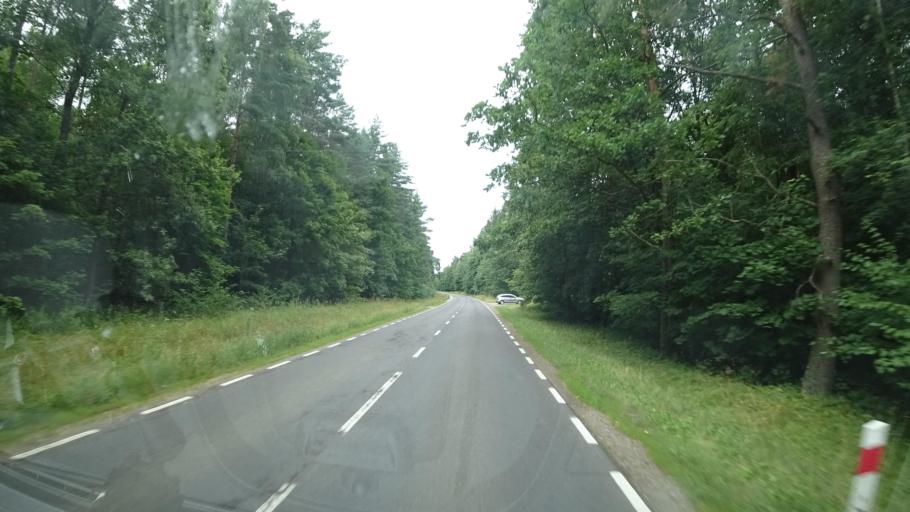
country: PL
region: Warmian-Masurian Voivodeship
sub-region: Powiat goldapski
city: Goldap
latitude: 54.3263
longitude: 22.2979
